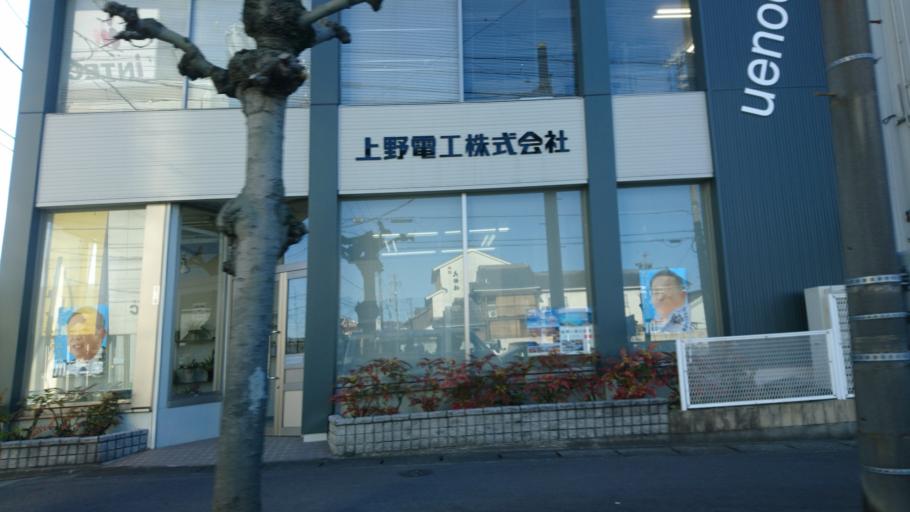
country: JP
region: Mie
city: Ueno-ebisumachi
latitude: 34.7586
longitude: 136.1324
